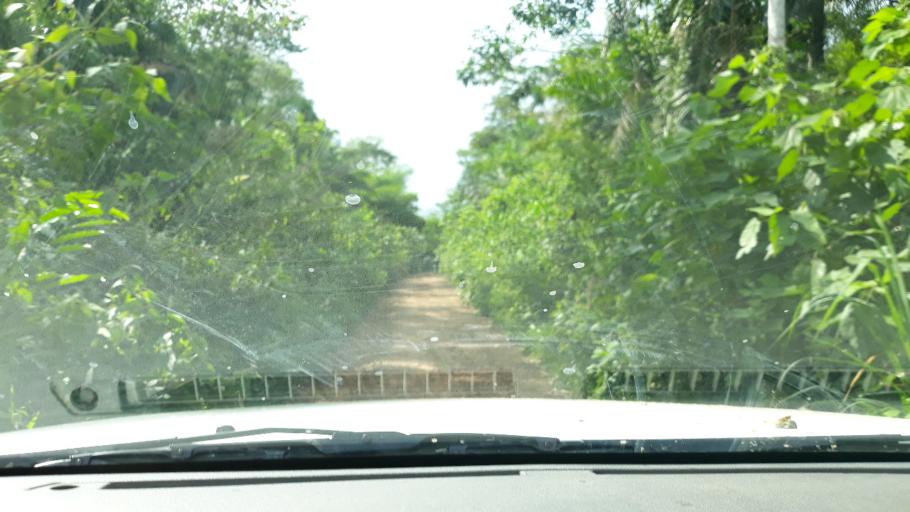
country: CD
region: Maniema
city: Kampene
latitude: -2.7690
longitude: 26.9311
